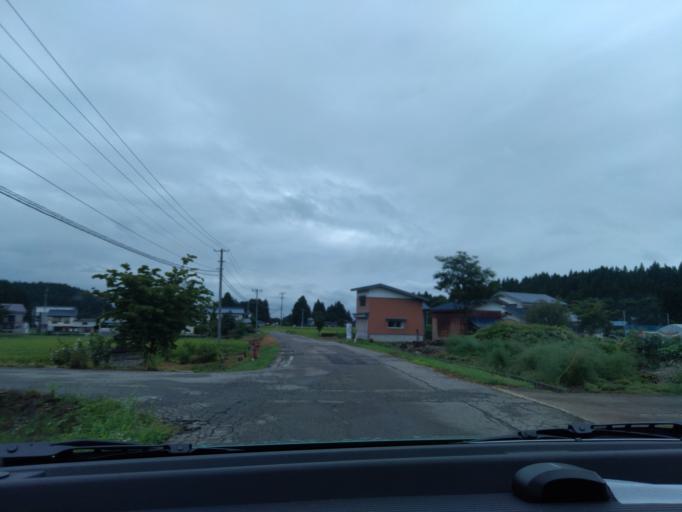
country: JP
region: Akita
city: Yokotemachi
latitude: 39.4202
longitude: 140.5952
